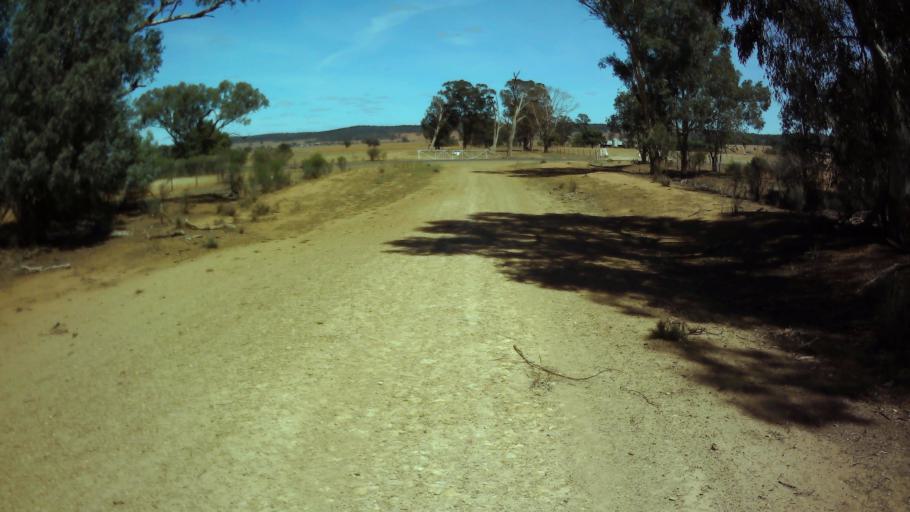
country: AU
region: New South Wales
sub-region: Forbes
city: Forbes
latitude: -33.7159
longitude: 147.8046
